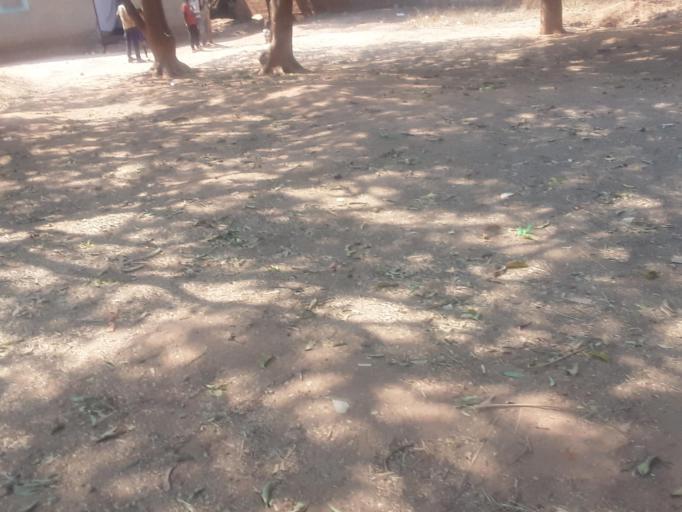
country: ZM
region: Lusaka
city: Lusaka
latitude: -15.3530
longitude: 28.2938
